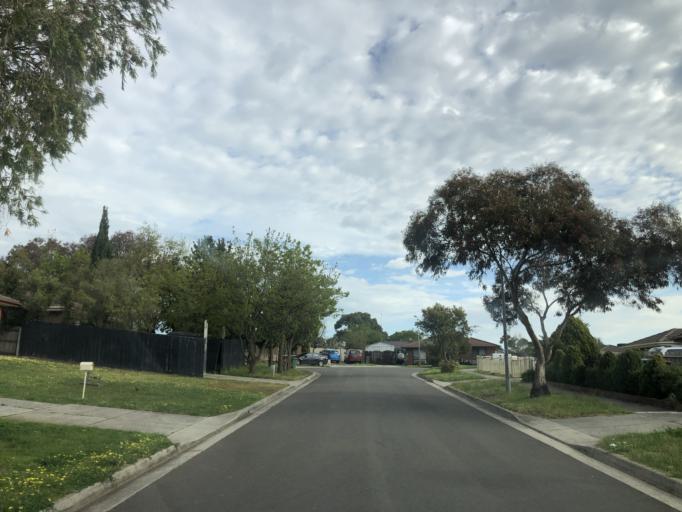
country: AU
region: Victoria
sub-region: Casey
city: Hampton Park
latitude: -38.0234
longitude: 145.2534
